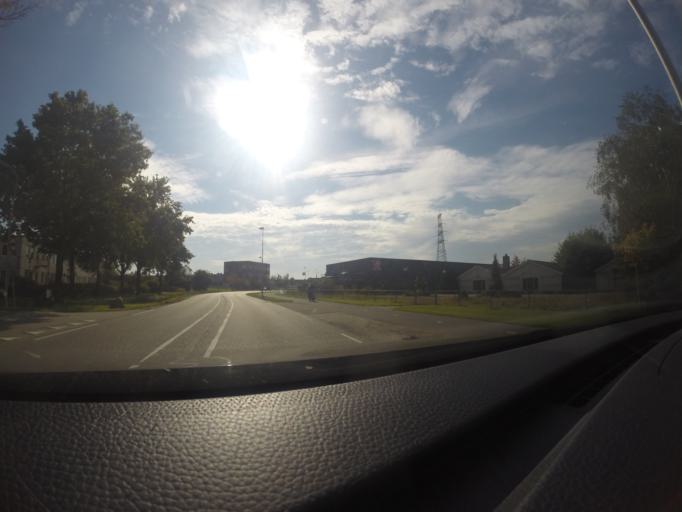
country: NL
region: Gelderland
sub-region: Gemeente Doetinchem
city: Doetinchem
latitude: 51.9490
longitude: 6.2859
